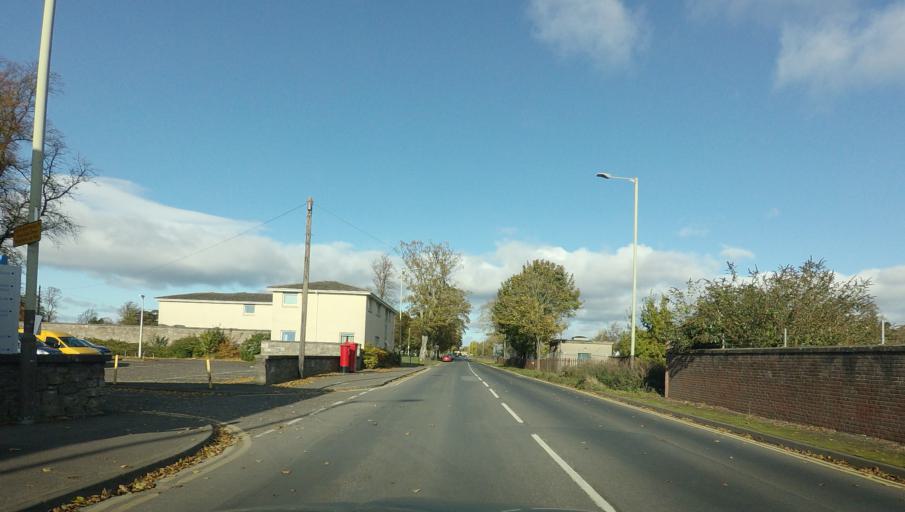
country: GB
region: Scotland
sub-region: Perth and Kinross
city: Perth
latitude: 56.3882
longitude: -3.4265
